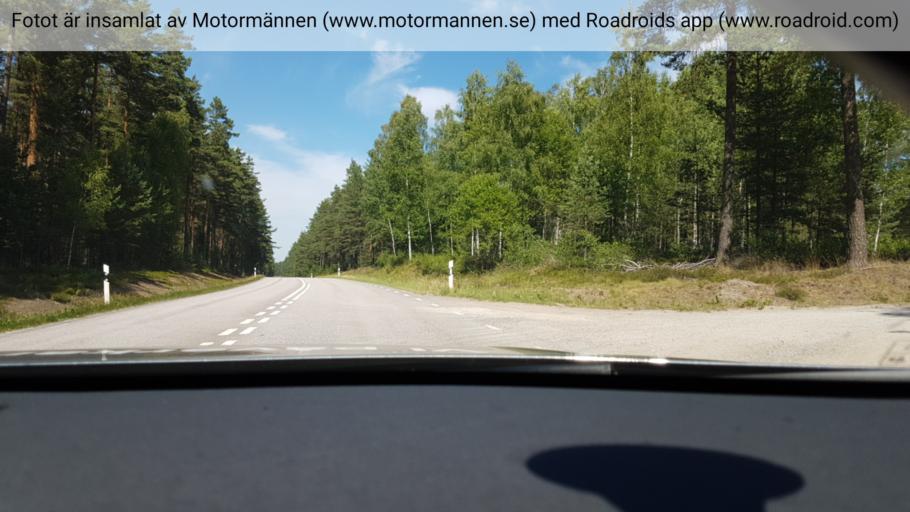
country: SE
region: Vaestra Goetaland
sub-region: Skovde Kommun
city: Stopen
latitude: 58.4538
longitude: 13.9548
